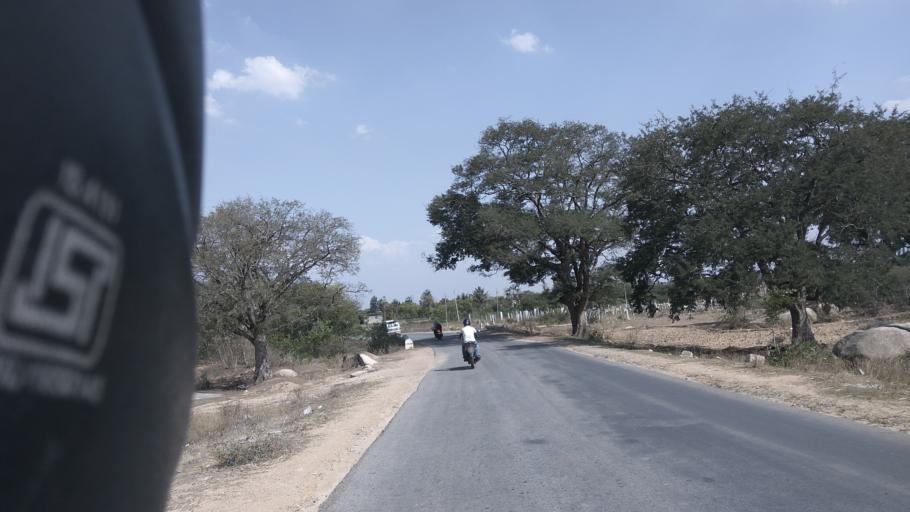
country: IN
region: Karnataka
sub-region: Kolar
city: Mulbagal
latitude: 13.1651
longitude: 78.3733
